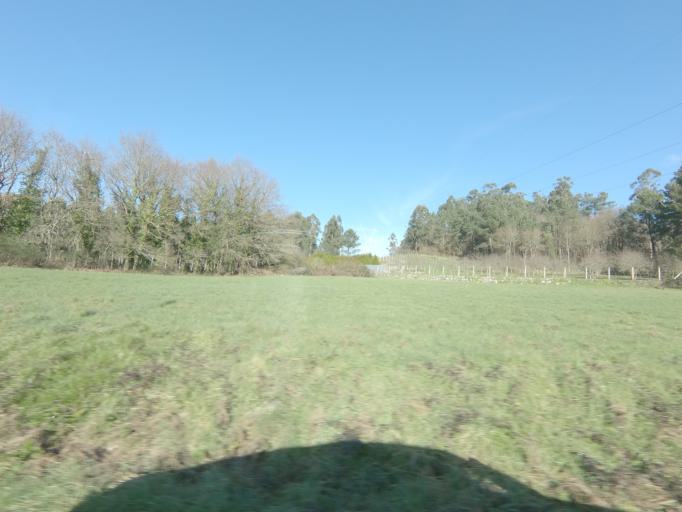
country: ES
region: Galicia
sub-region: Provincia da Coruna
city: Ribeira
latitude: 42.7112
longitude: -8.4324
